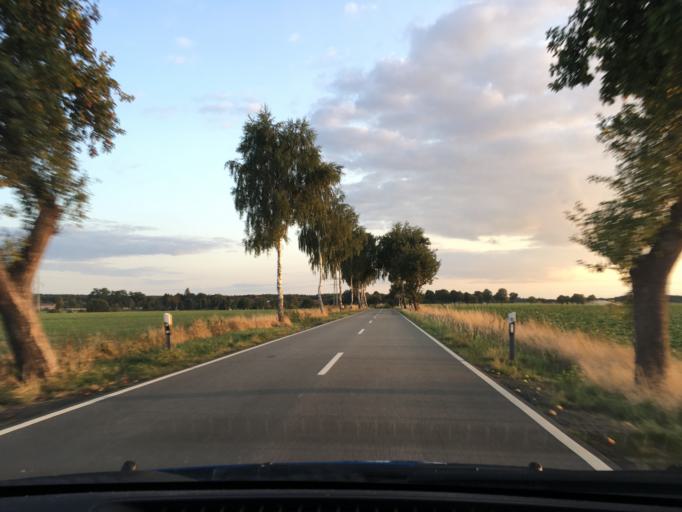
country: DE
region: Lower Saxony
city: Nahrendorf
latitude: 53.1664
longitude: 10.8104
